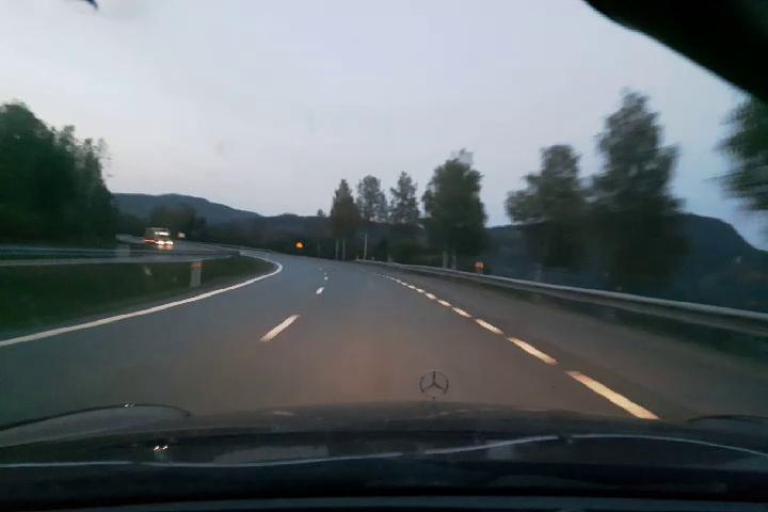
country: SE
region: Vaesternorrland
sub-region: Kramfors Kommun
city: Nordingra
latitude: 63.0117
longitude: 18.2908
